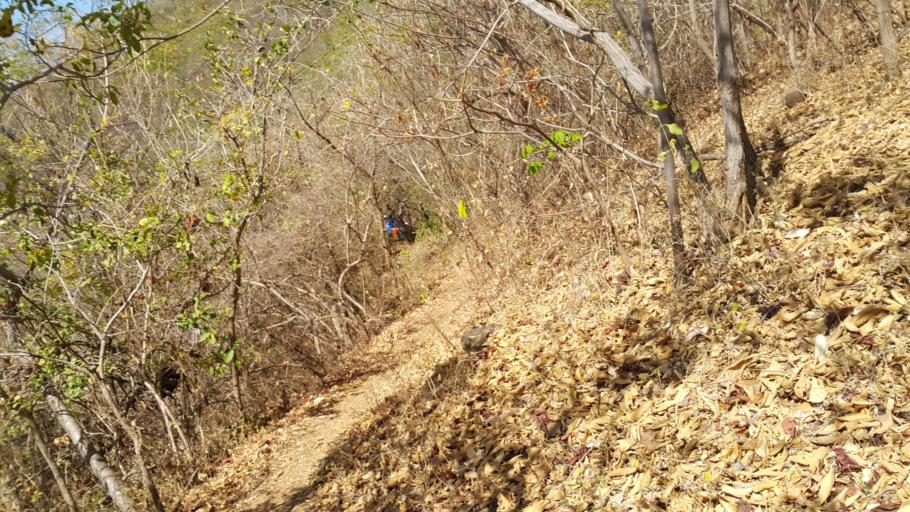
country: NI
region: Leon
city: La Paz Centro
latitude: 12.4493
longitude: -86.6667
